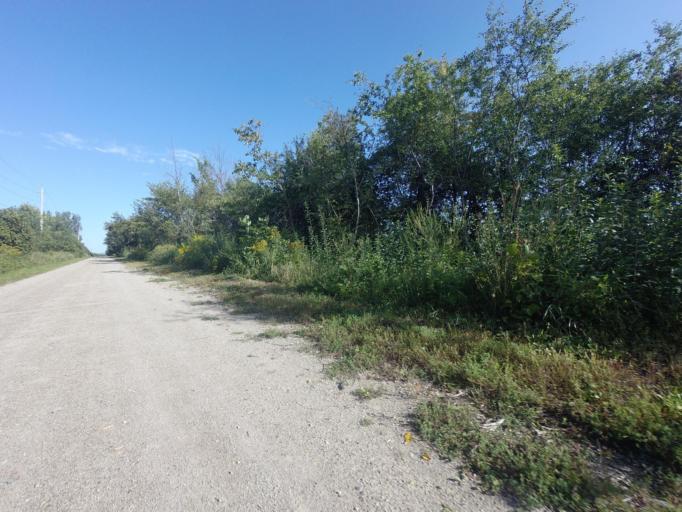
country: CA
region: Ontario
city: Waterloo
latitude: 43.6671
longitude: -80.4383
